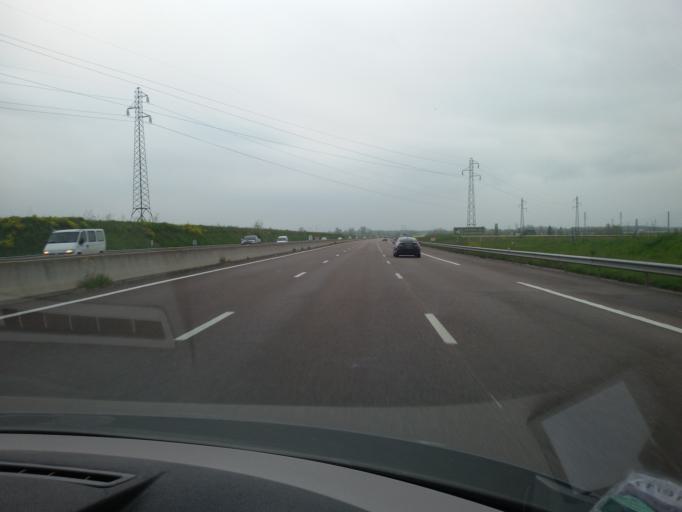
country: FR
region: Bourgogne
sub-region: Departement de la Cote-d'Or
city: Nuits-Saint-Georges
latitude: 47.0843
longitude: 4.9323
